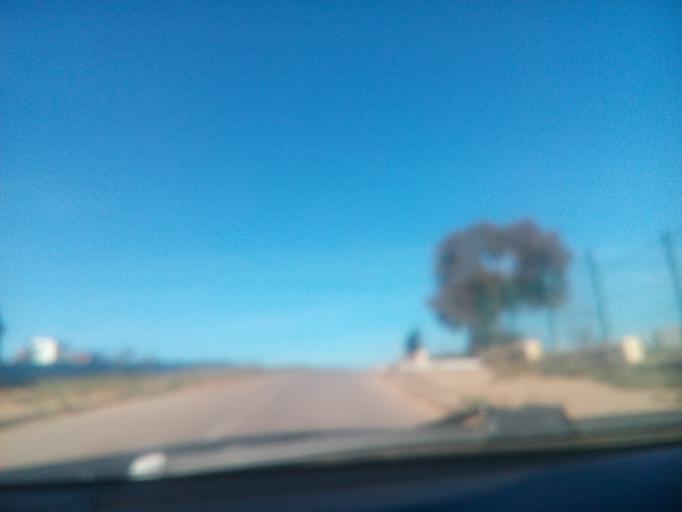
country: DZ
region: Oran
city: Bir el Djir
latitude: 35.7296
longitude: -0.5411
